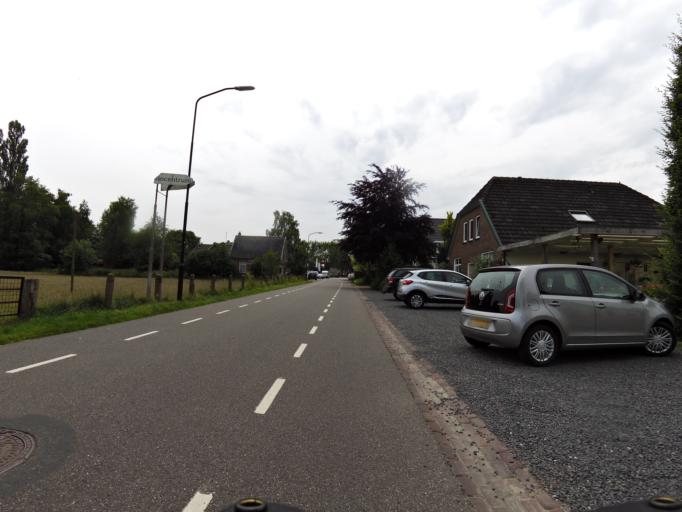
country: NL
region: Gelderland
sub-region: Gemeente Apeldoorn
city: Beekbergen
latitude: 52.1635
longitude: 5.9897
